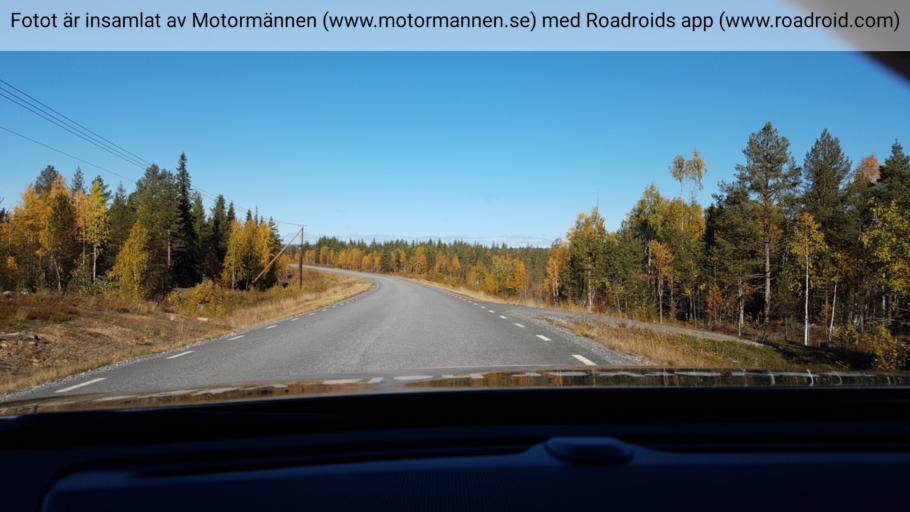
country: SE
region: Norrbotten
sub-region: Gallivare Kommun
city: Gaellivare
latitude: 66.7742
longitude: 21.0528
